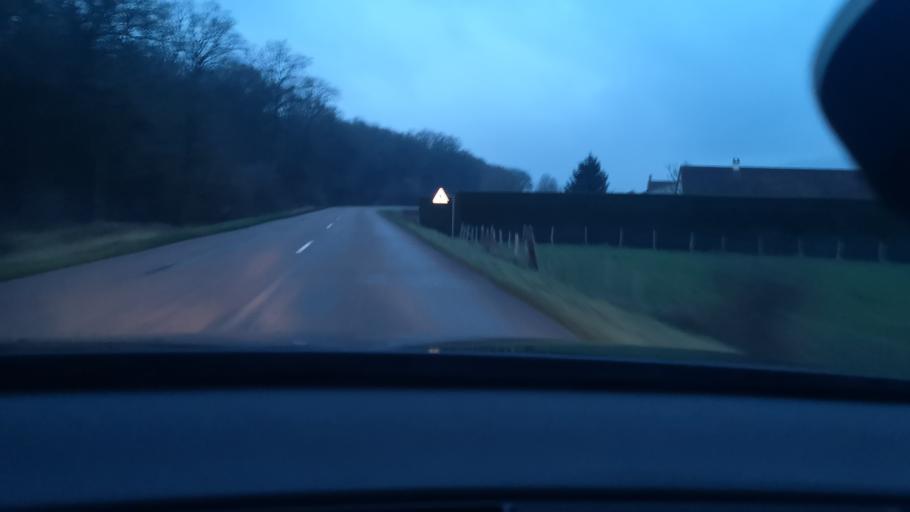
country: FR
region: Bourgogne
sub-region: Departement de Saone-et-Loire
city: Demigny
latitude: 46.9440
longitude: 4.8780
